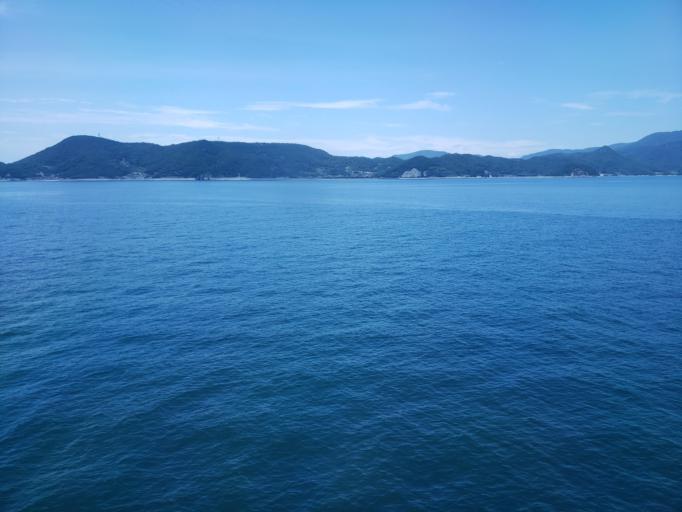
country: JP
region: Kagawa
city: Tonosho
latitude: 34.4218
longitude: 134.2687
